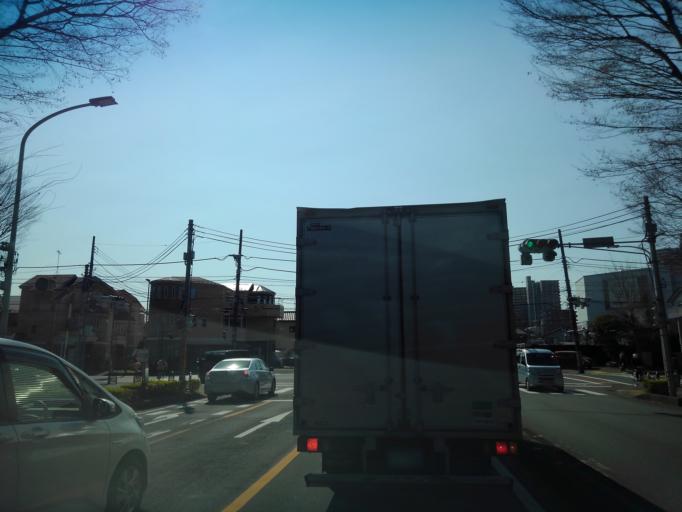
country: JP
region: Saitama
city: Tokorozawa
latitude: 35.7951
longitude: 139.4712
